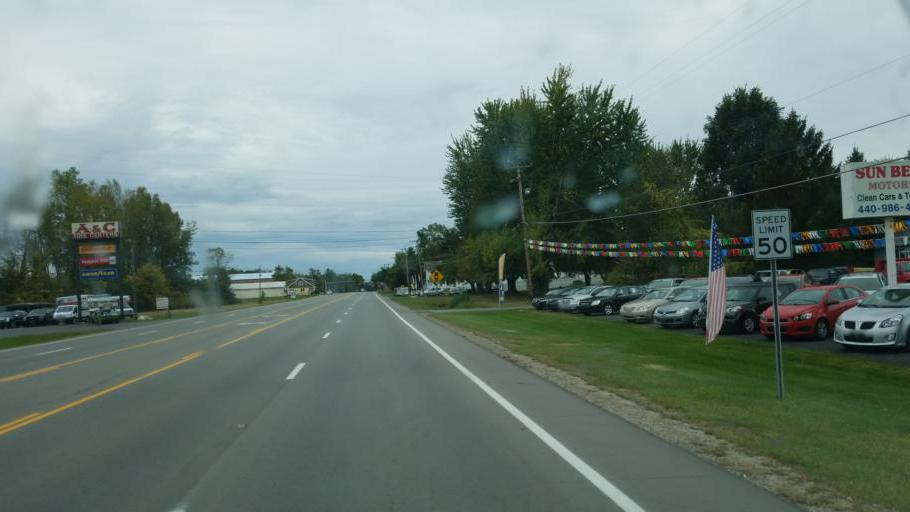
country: US
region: Ohio
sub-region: Lorain County
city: Amherst
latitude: 41.3704
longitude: -82.2105
